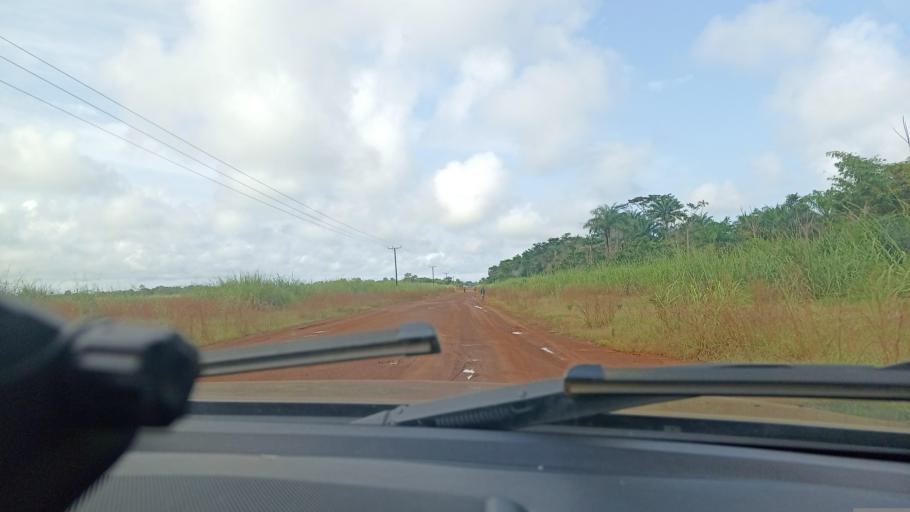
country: LR
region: Grand Cape Mount
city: Robertsport
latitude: 6.6979
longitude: -11.0991
